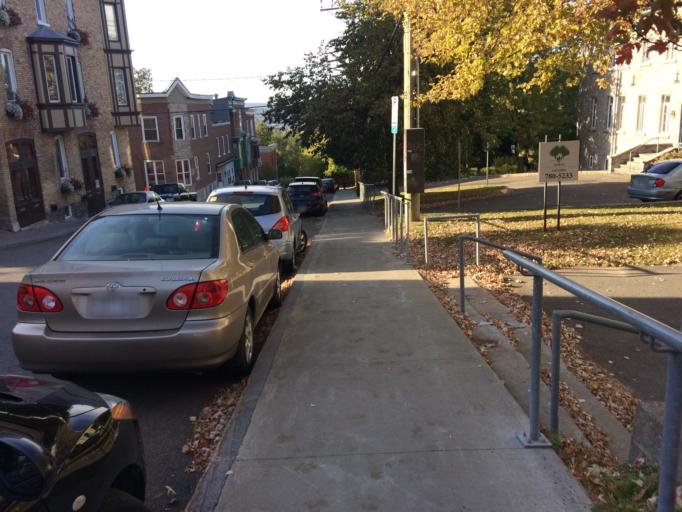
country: CA
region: Quebec
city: Quebec
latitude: 46.8049
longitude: -71.2329
